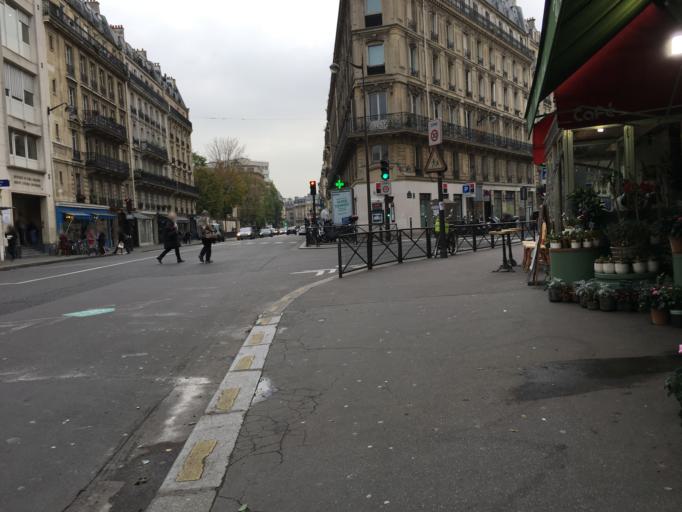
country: FR
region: Ile-de-France
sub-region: Paris
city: Paris
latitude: 48.8444
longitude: 2.3420
